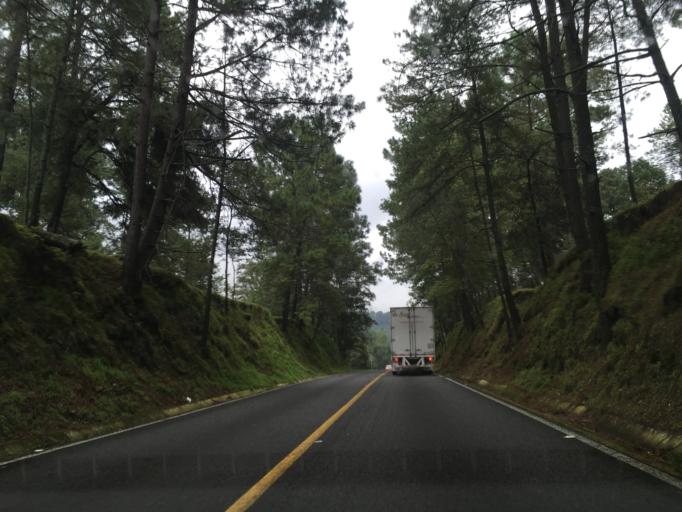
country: MX
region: Michoacan
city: Tingambato
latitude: 19.4780
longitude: -101.9010
